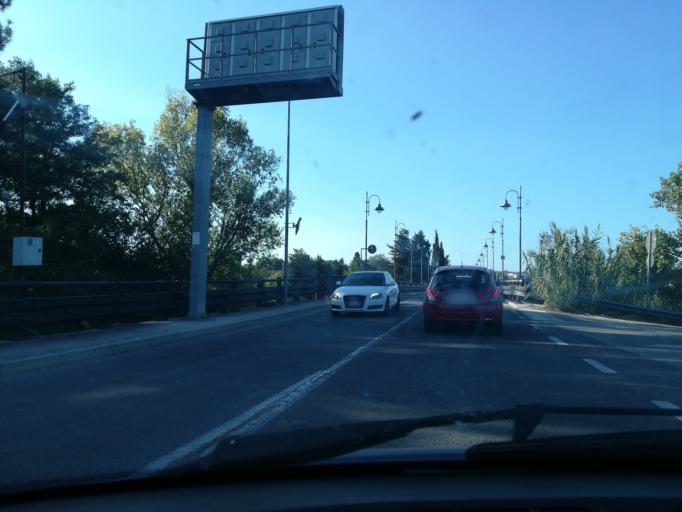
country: IT
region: The Marches
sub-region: Provincia di Macerata
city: Villa Potenza
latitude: 43.3266
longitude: 13.4269
